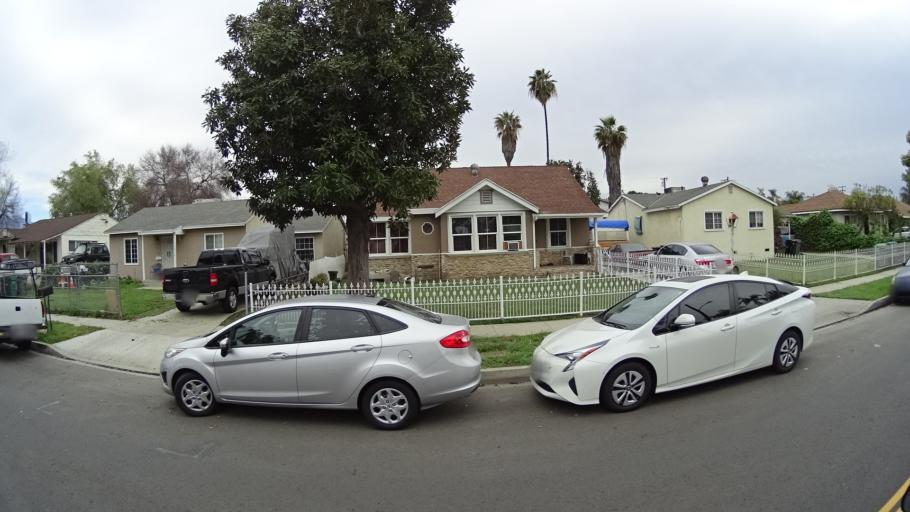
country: US
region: California
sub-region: Los Angeles County
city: West Puente Valley
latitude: 34.0651
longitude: -117.9913
